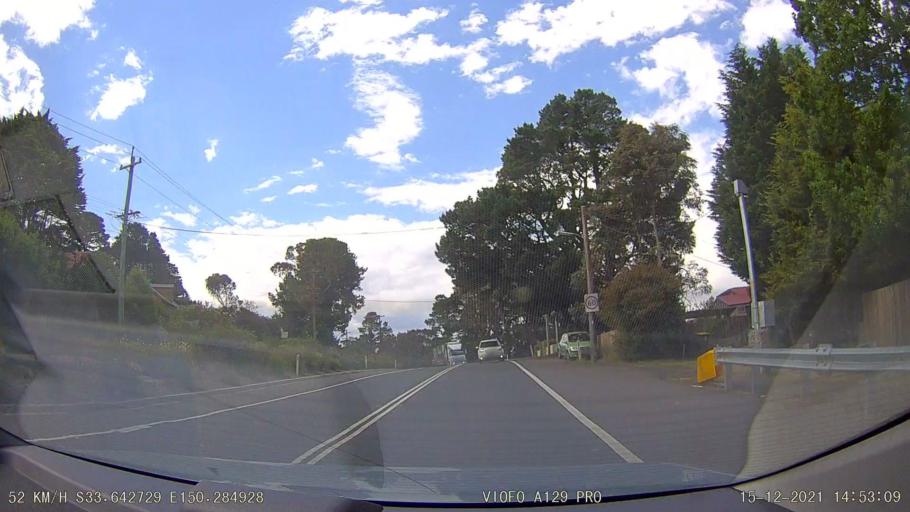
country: AU
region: New South Wales
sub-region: Blue Mountains Municipality
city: Blackheath
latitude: -33.6428
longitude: 150.2846
